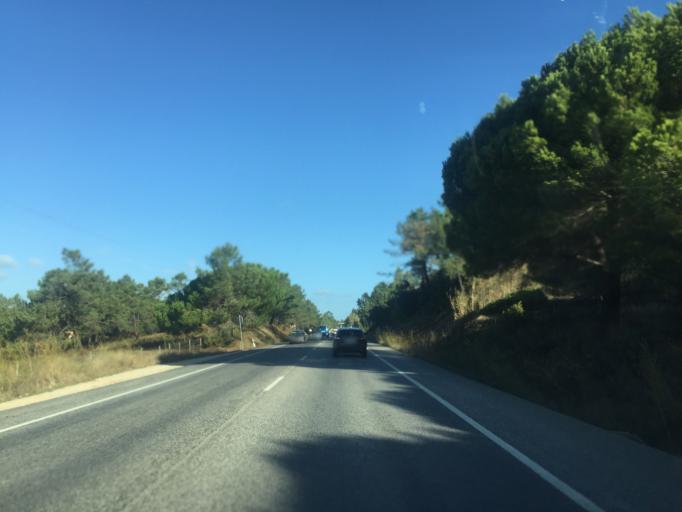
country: PT
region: Lisbon
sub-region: Azambuja
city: Alcoentre
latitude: 39.2173
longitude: -8.9538
